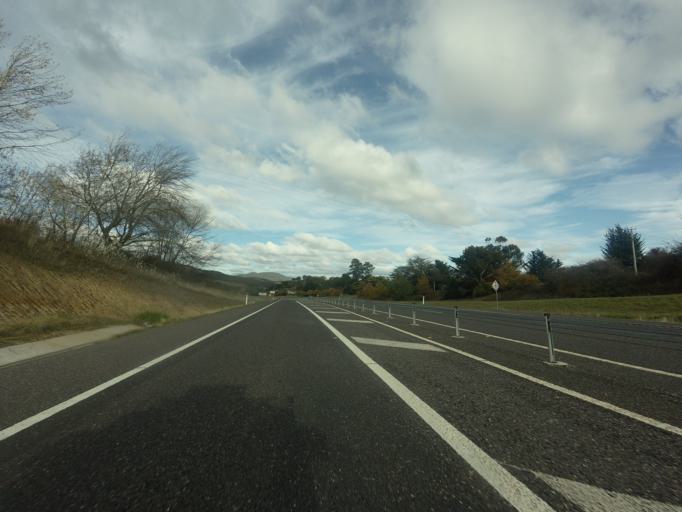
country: AU
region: Tasmania
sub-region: Brighton
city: Bridgewater
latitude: -42.5717
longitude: 147.2132
